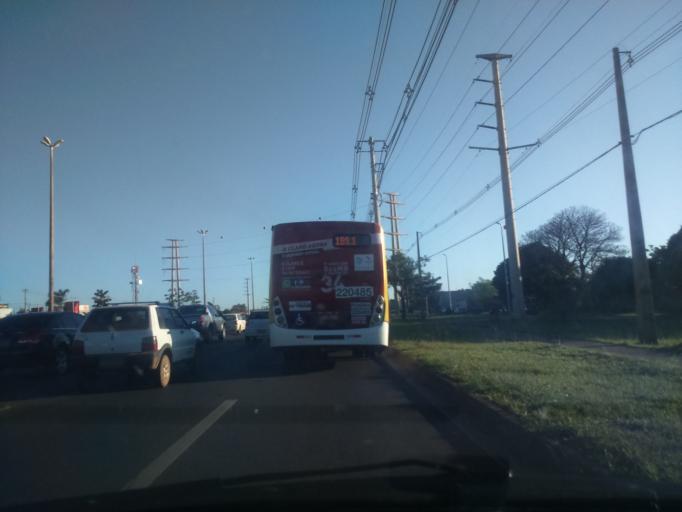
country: BR
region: Federal District
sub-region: Brasilia
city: Brasilia
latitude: -15.8764
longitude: -47.8230
